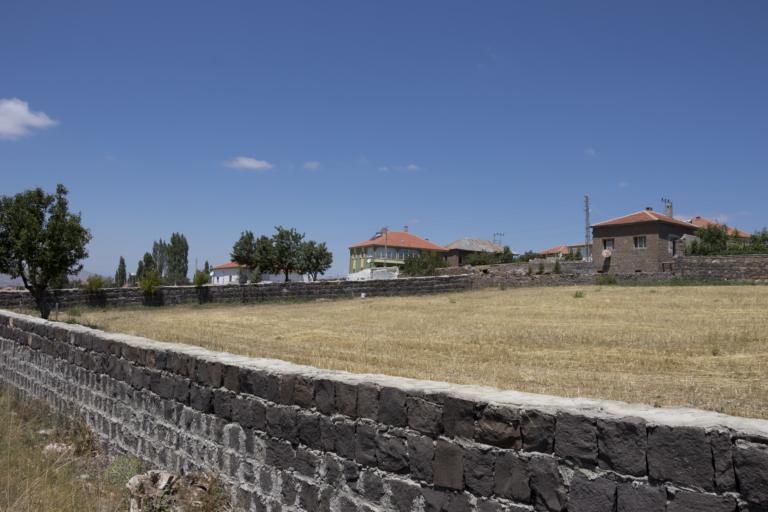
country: TR
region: Kayseri
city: Toklar
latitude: 38.4061
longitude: 36.0790
